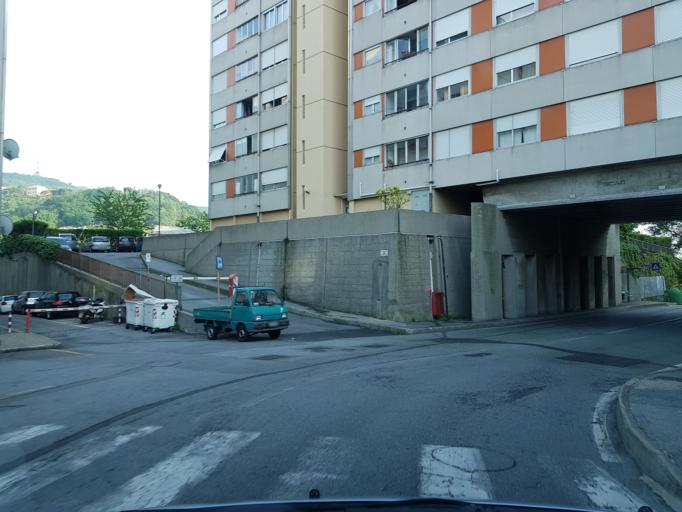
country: IT
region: Liguria
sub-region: Provincia di Genova
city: Genoa
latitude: 44.4435
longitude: 8.9012
